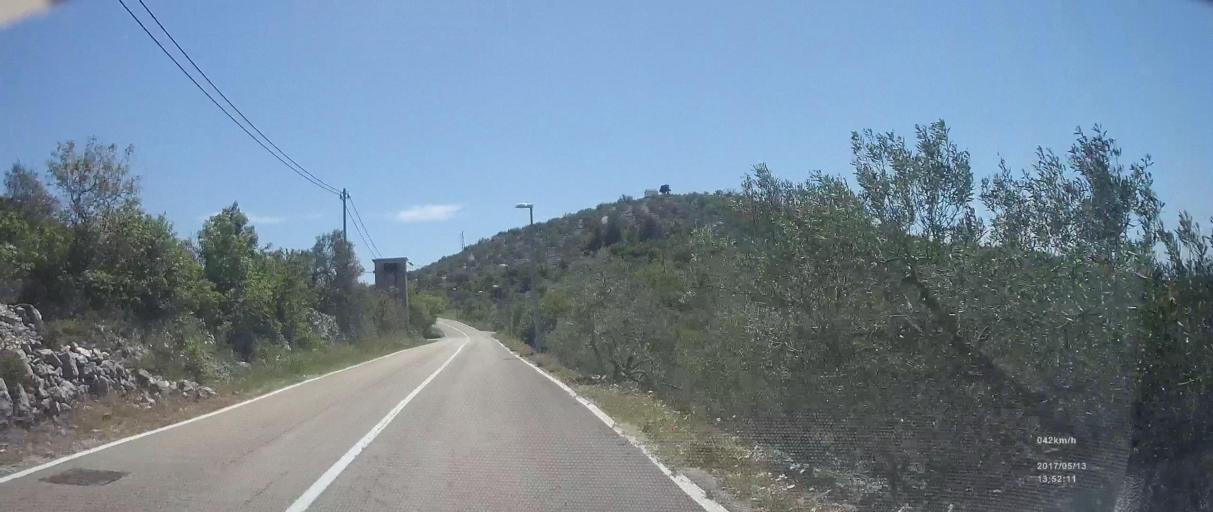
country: HR
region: Sibensko-Kniniska
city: Primosten
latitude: 43.6085
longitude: 15.9958
